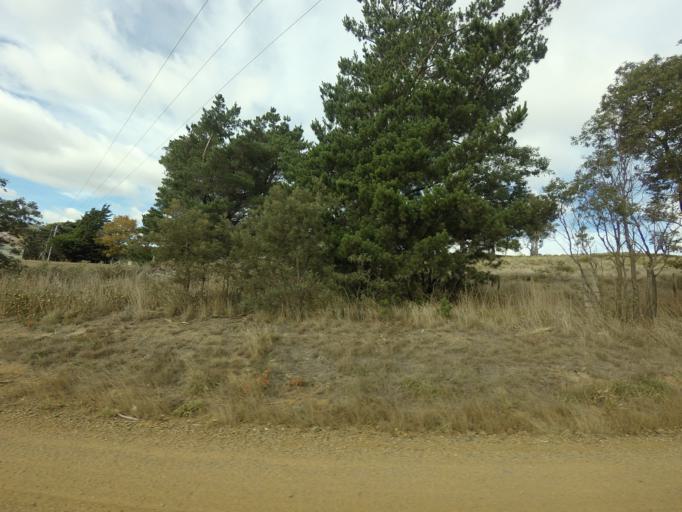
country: AU
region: Tasmania
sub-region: Brighton
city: Bridgewater
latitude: -42.4105
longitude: 147.4001
